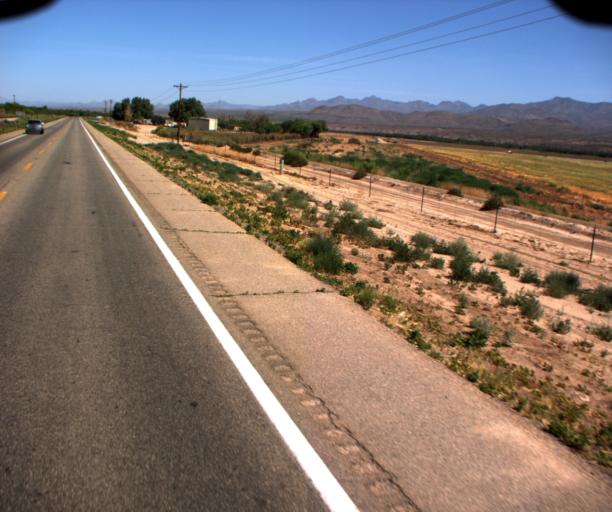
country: US
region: Arizona
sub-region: Graham County
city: Pima
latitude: 33.0168
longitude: -109.9527
